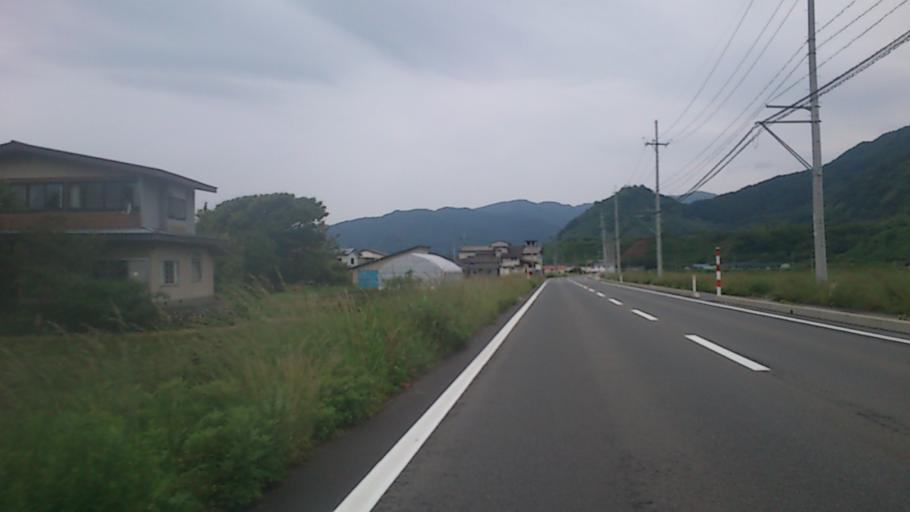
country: JP
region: Akita
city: Noshiromachi
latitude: 40.3455
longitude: 140.0284
